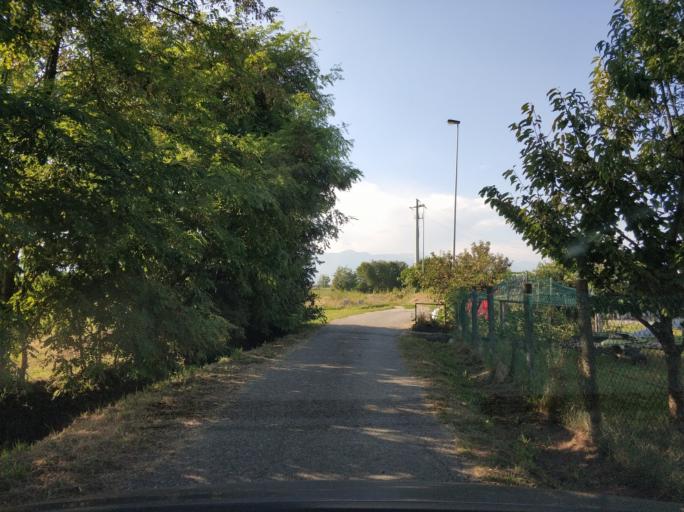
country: IT
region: Piedmont
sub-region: Provincia di Torino
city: San Maurizio
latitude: 45.2035
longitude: 7.6121
